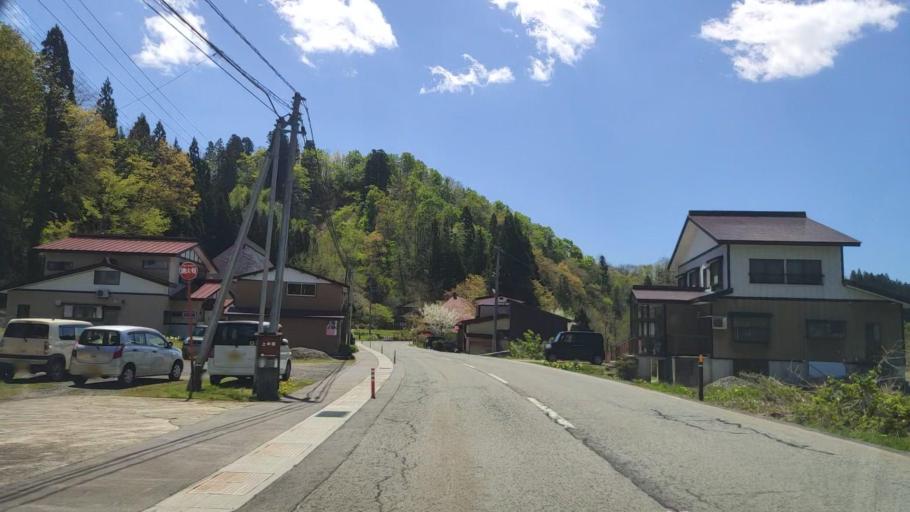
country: JP
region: Yamagata
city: Shinjo
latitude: 38.9252
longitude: 140.3415
